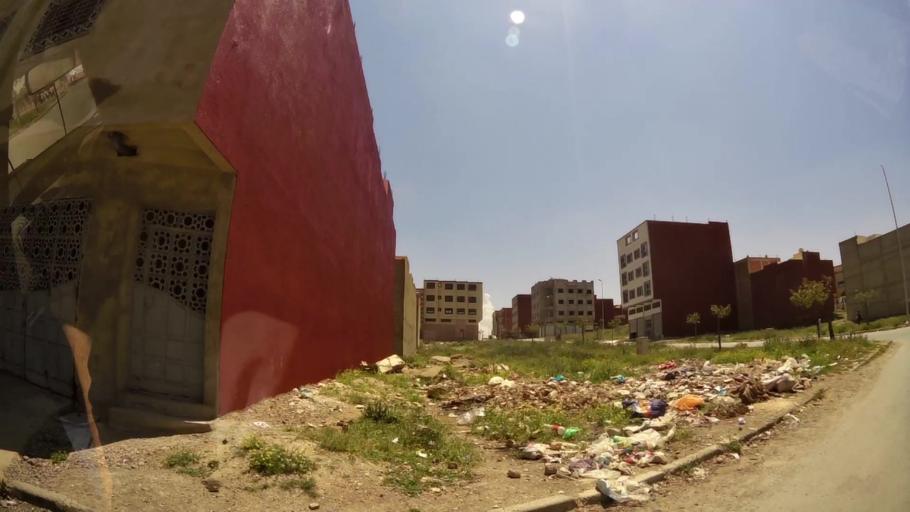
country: MA
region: Oriental
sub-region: Oujda-Angad
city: Oujda
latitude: 34.6811
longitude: -1.9504
